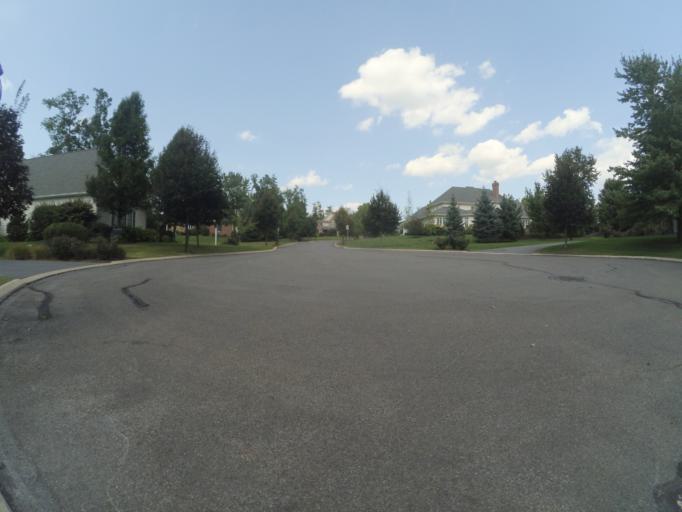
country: US
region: Pennsylvania
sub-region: Centre County
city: Houserville
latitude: 40.8240
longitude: -77.8203
